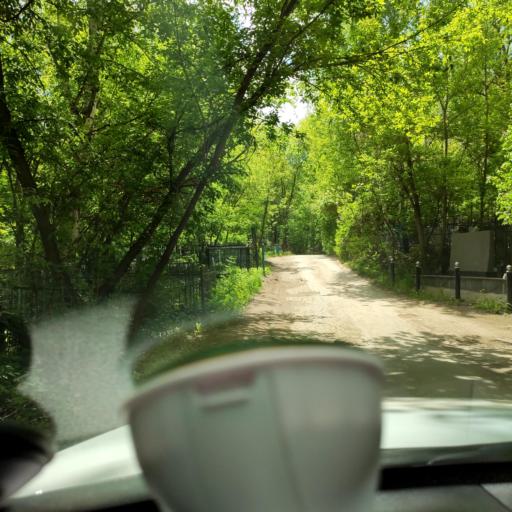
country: RU
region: Samara
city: Petra-Dubrava
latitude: 53.2758
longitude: 50.3230
